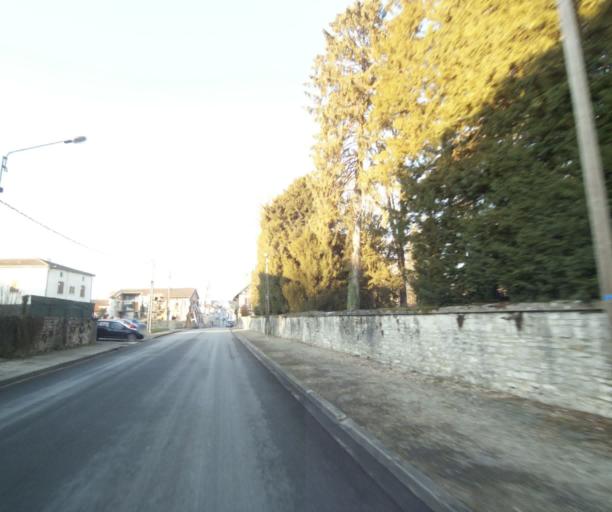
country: FR
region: Champagne-Ardenne
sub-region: Departement de la Haute-Marne
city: Bienville
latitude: 48.5820
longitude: 5.0394
